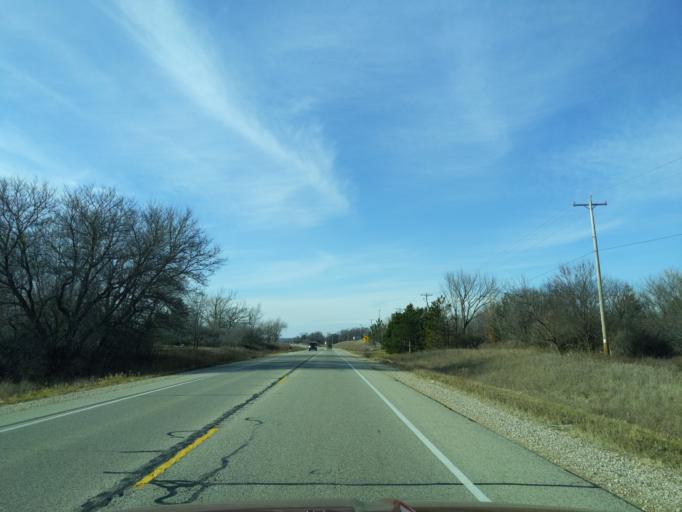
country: US
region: Wisconsin
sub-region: Walworth County
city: Whitewater
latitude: 42.8066
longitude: -88.6636
